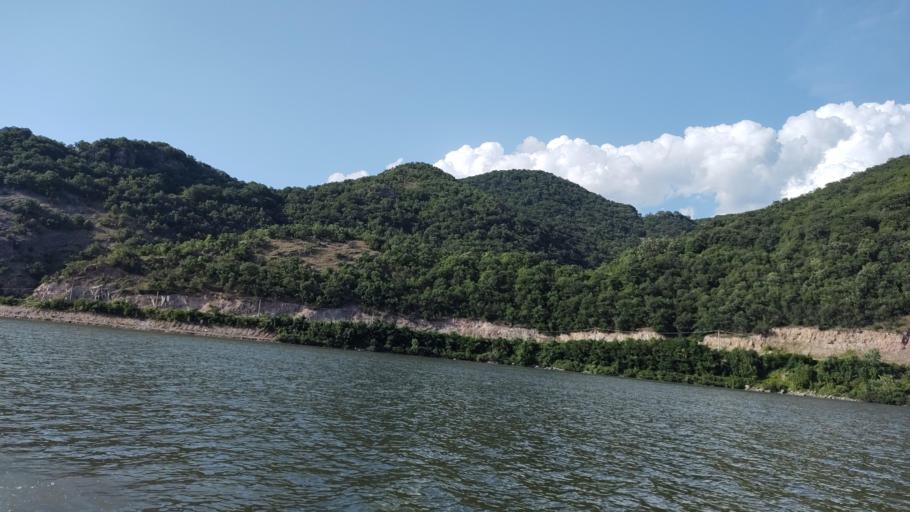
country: RO
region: Mehedinti
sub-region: Comuna Svinita
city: Svinita
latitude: 44.5440
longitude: 22.0456
